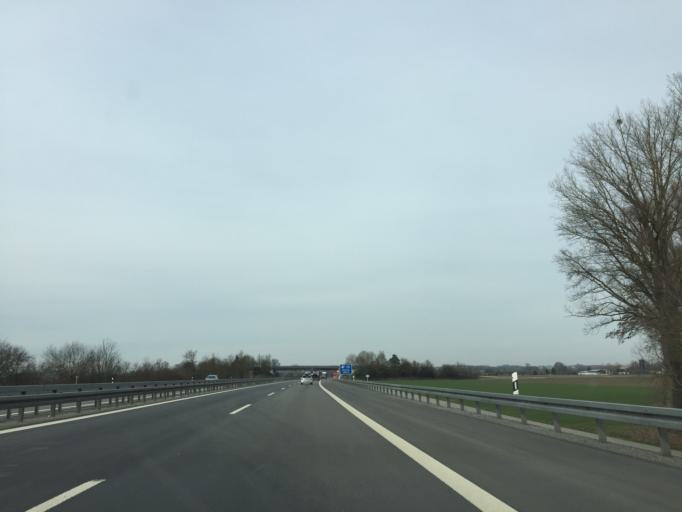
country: AT
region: Upper Austria
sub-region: Politischer Bezirk Scharding
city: Scharding
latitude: 48.4243
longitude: 13.3894
